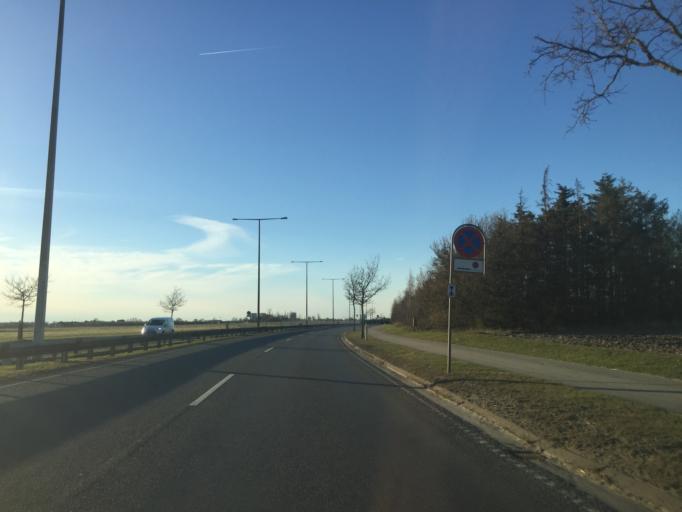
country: DK
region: Capital Region
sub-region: Tarnby Kommune
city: Tarnby
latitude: 55.5984
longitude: 12.6252
